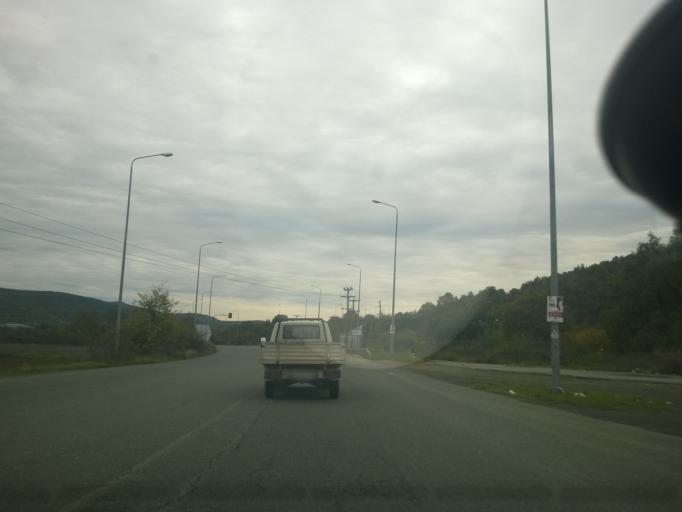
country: GR
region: Central Macedonia
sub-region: Nomos Pellis
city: Apsalos
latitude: 40.8882
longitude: 22.0680
